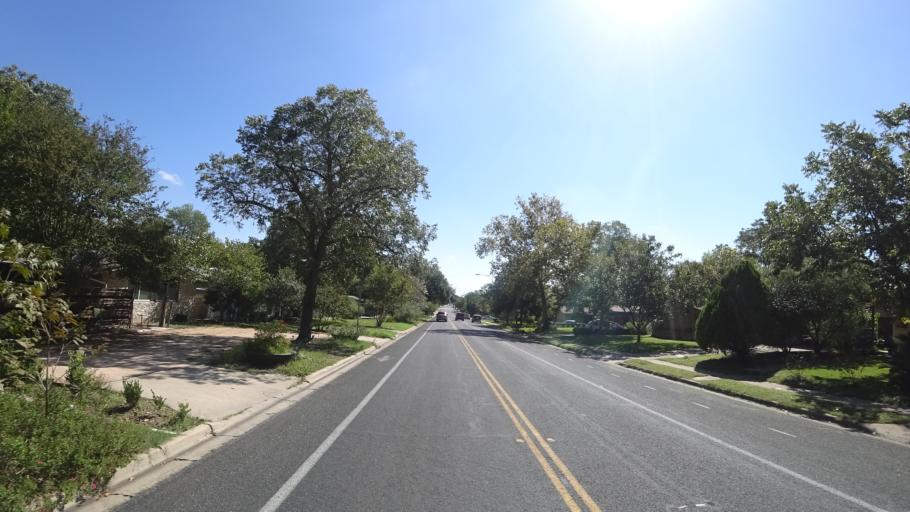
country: US
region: Texas
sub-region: Travis County
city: Austin
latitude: 30.3159
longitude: -97.6963
